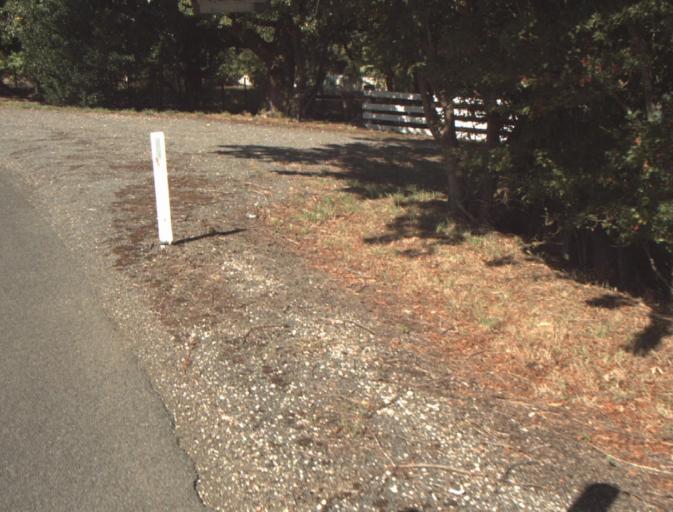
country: AU
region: Tasmania
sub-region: Launceston
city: Mayfield
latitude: -41.2414
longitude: 147.2305
